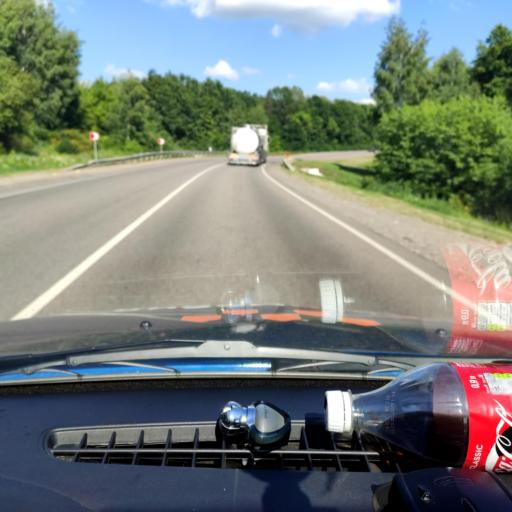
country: RU
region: Lipetsk
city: Kazaki
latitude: 52.6370
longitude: 38.2995
